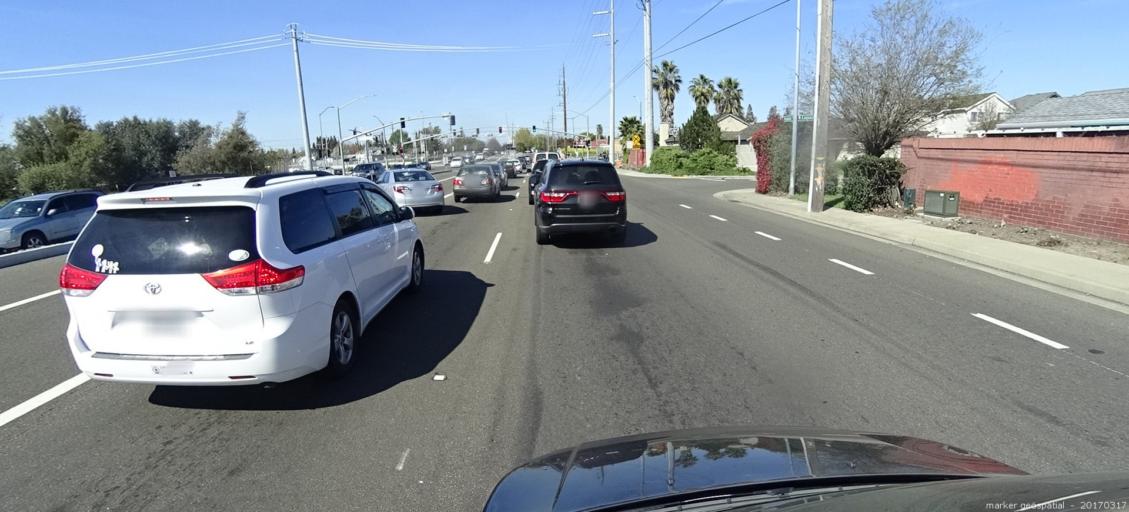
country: US
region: California
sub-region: Sacramento County
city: Parkway
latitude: 38.4614
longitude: -121.4464
